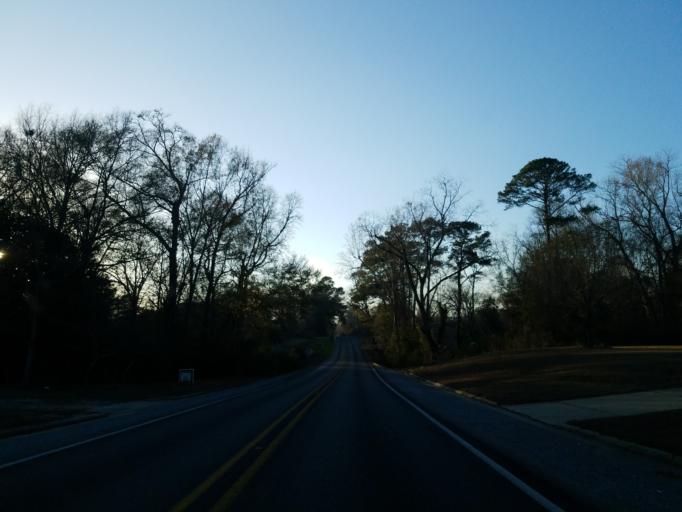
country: US
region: Mississippi
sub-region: Clarke County
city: Stonewall
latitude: 32.1758
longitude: -88.8220
